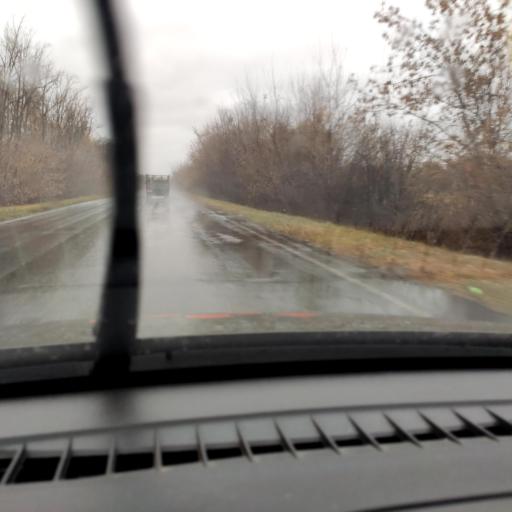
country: RU
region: Samara
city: Tol'yatti
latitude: 53.6922
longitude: 49.2486
